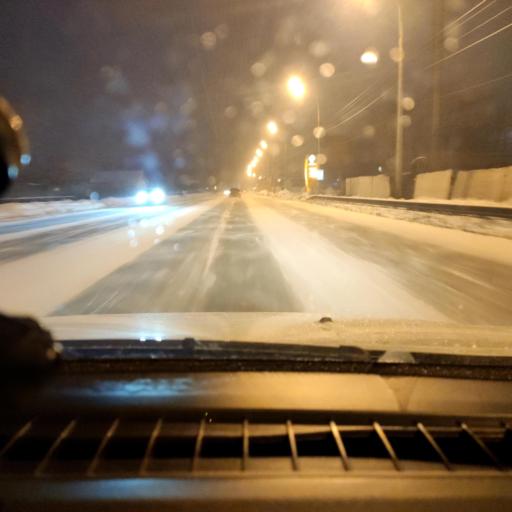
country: RU
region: Samara
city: Otradnyy
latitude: 53.3589
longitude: 51.3445
